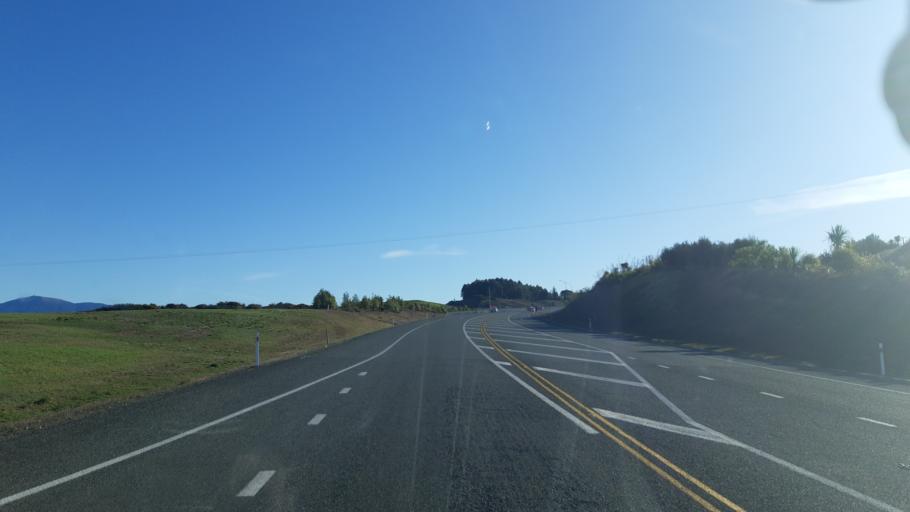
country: NZ
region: Tasman
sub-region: Tasman District
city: Mapua
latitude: -41.2448
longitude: 173.0558
